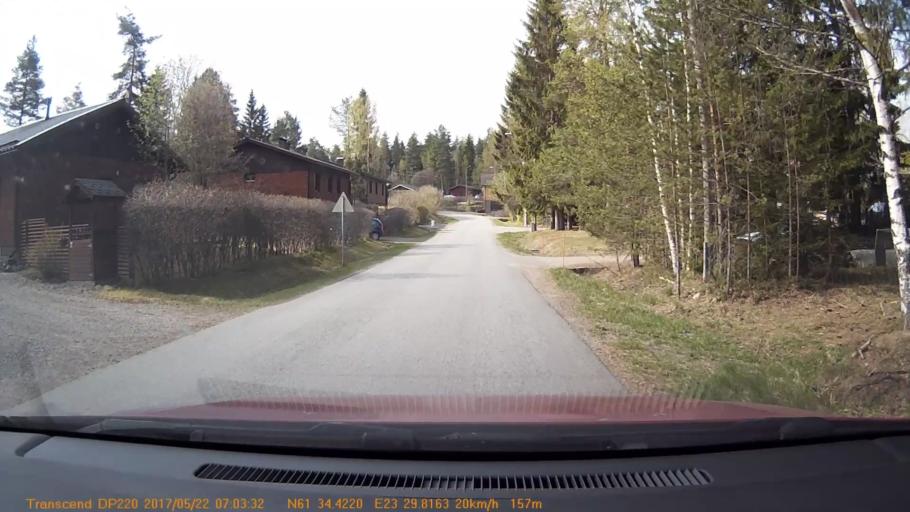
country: FI
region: Pirkanmaa
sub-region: Tampere
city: Yloejaervi
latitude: 61.5738
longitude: 23.4969
